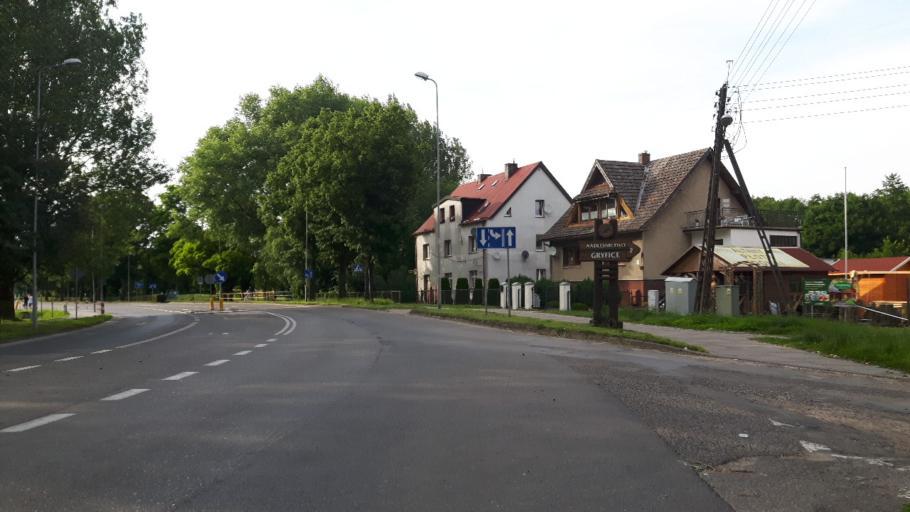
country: PL
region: West Pomeranian Voivodeship
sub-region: Powiat gryficki
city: Gryfice
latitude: 53.9096
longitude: 15.2003
